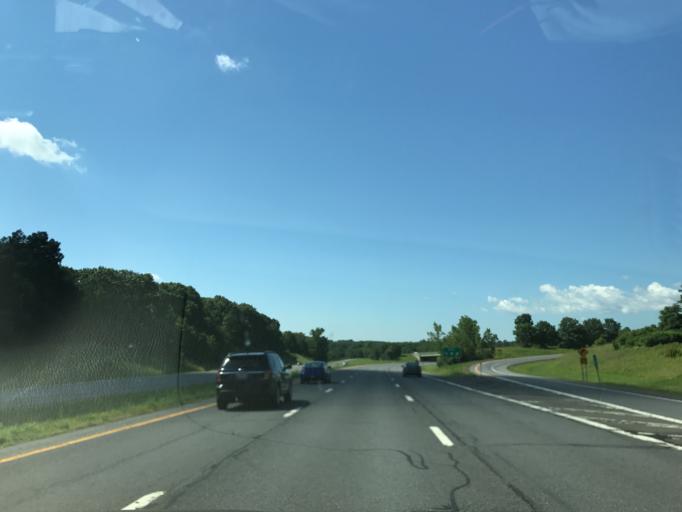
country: US
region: New York
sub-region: Rensselaer County
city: East Greenbush
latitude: 42.5634
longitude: -73.6789
